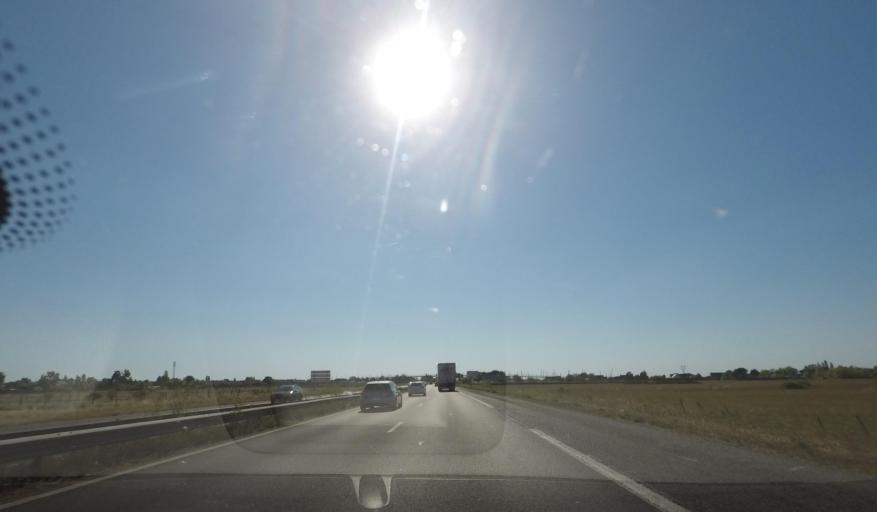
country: FR
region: Pays de la Loire
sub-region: Departement de la Loire-Atlantique
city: Trignac
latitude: 47.3240
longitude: -2.1774
